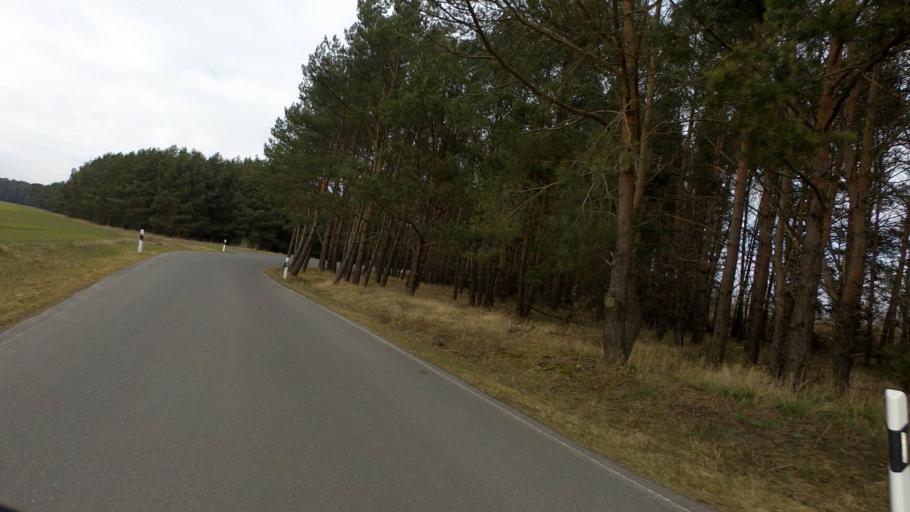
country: DE
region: Brandenburg
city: Ludwigsfelde
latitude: 52.2705
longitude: 13.2659
